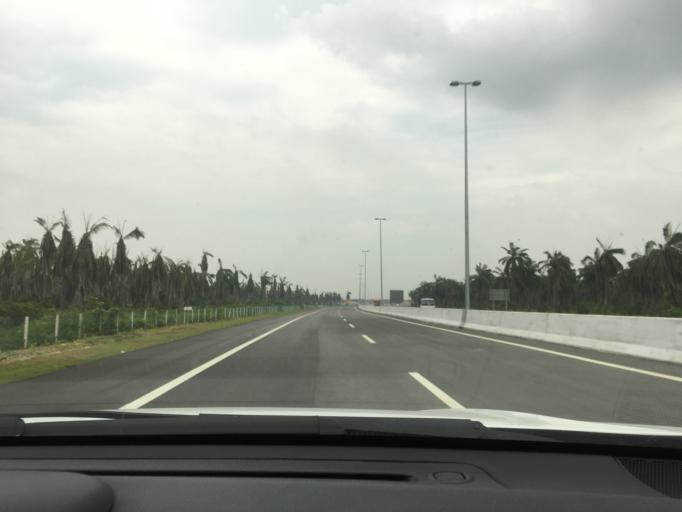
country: MY
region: Selangor
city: Klang
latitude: 3.1014
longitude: 101.4216
